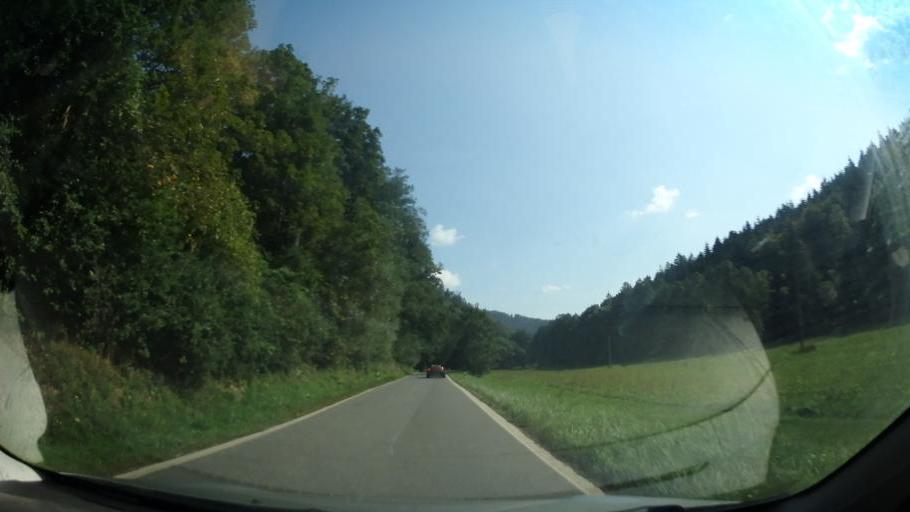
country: CZ
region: South Moravian
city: Olesnice
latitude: 49.5393
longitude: 16.3418
